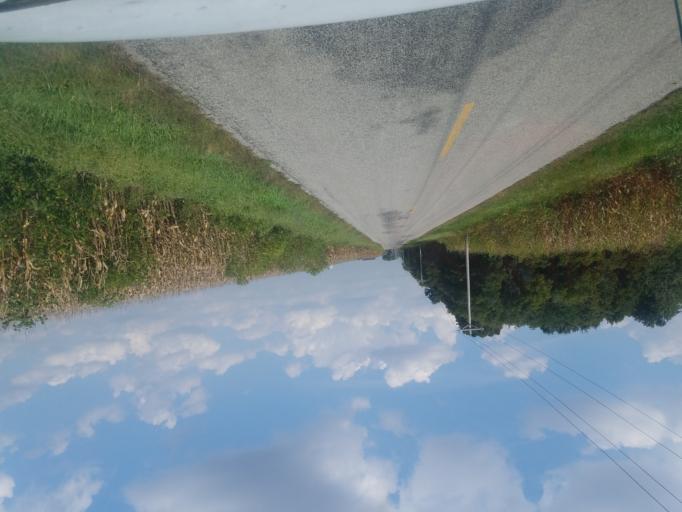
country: US
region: Ohio
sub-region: Hardin County
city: Ada
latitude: 40.6361
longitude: -83.7790
